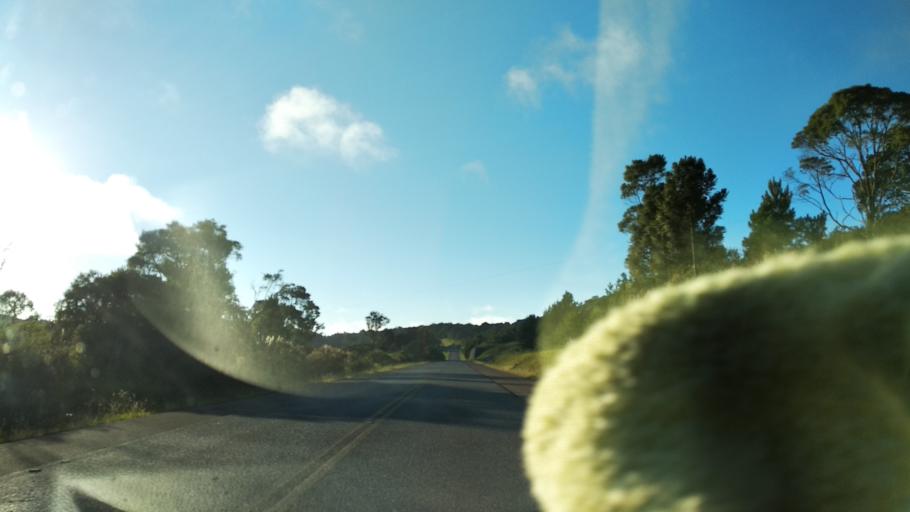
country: BR
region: Santa Catarina
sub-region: Correia Pinto
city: Correia Pinto
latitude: -27.6143
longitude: -50.6915
